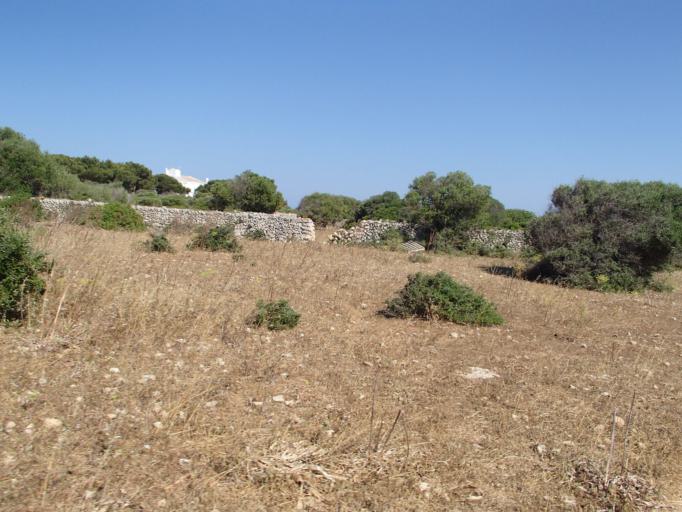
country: ES
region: Balearic Islands
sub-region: Illes Balears
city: Es Castell
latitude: 39.8461
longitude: 4.2933
